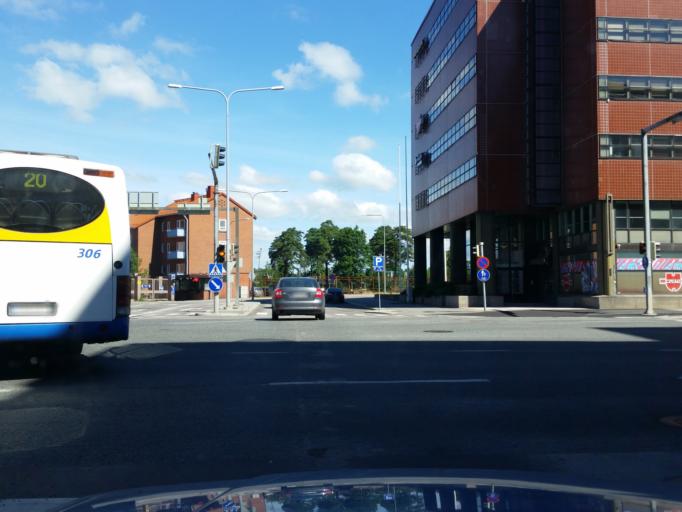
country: FI
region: Uusimaa
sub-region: Helsinki
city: Helsinki
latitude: 60.1640
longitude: 24.9078
